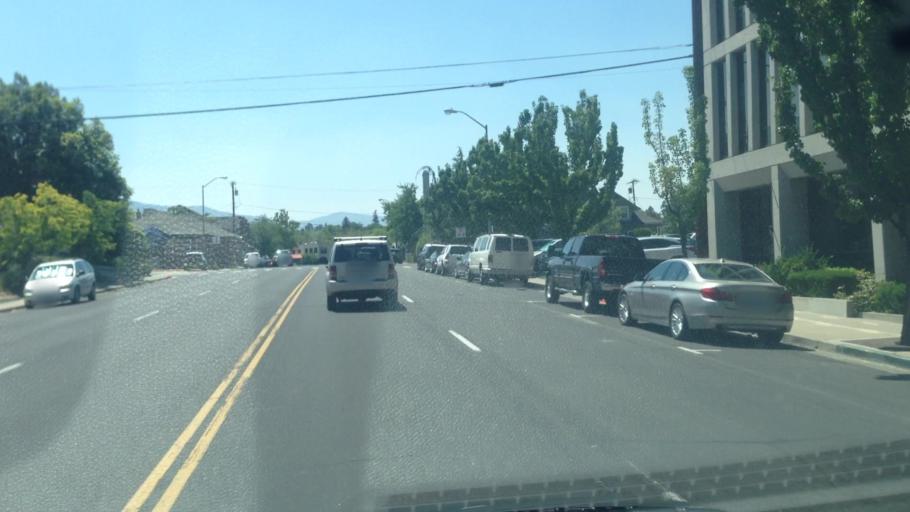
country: US
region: Nevada
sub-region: Washoe County
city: Reno
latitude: 39.5212
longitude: -119.8142
